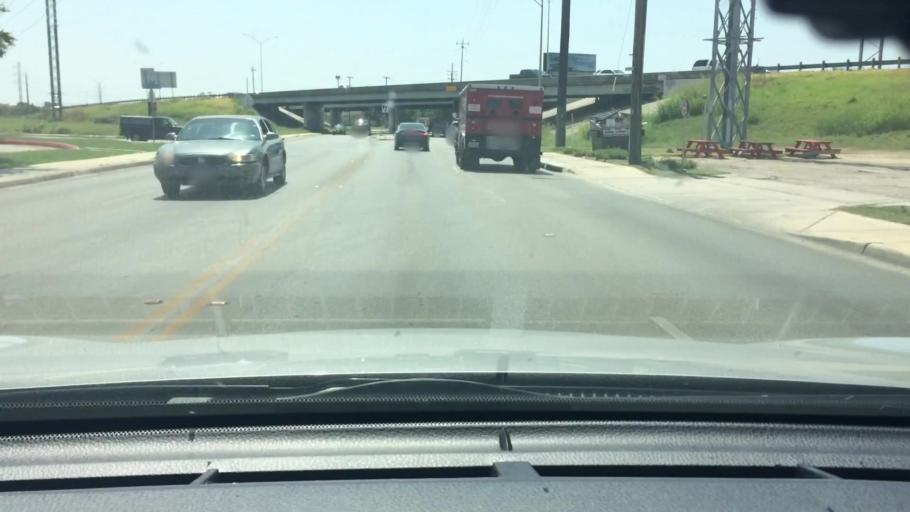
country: US
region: Texas
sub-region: Bexar County
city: San Antonio
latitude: 29.3611
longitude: -98.4371
